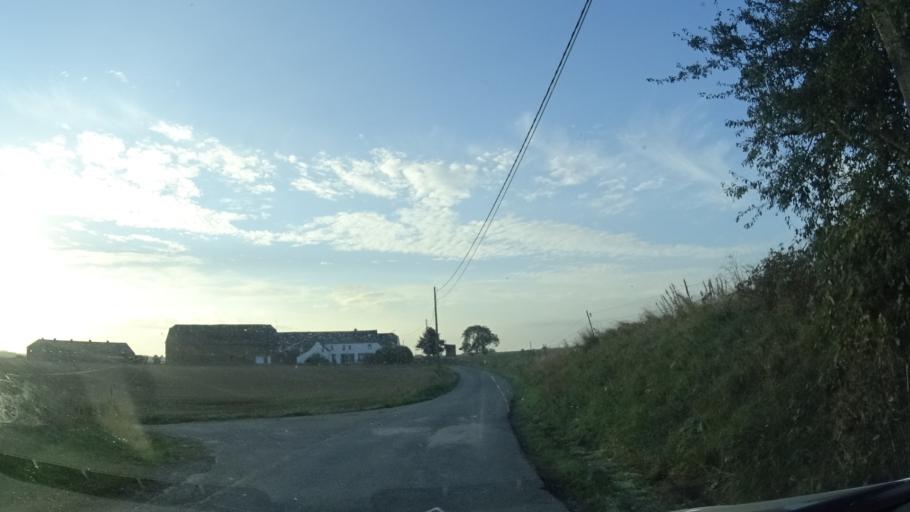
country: BE
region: Wallonia
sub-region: Province du Hainaut
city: Beaumont
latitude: 50.2470
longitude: 4.2635
